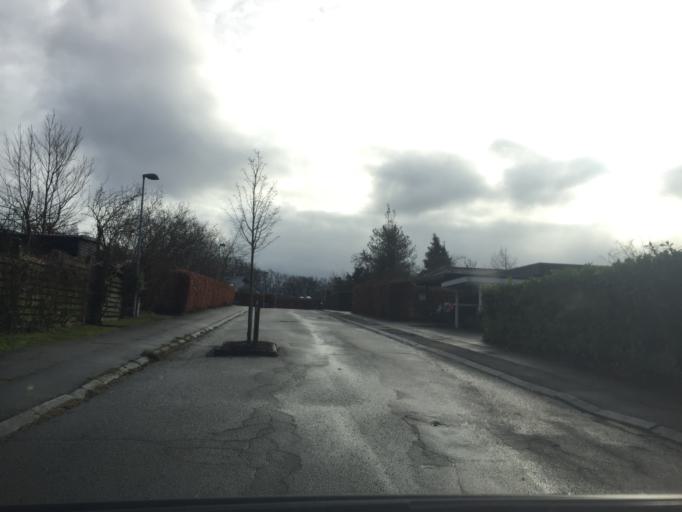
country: DK
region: Capital Region
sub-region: Fureso Kommune
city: Stavnsholt
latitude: 55.8109
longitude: 12.3996
